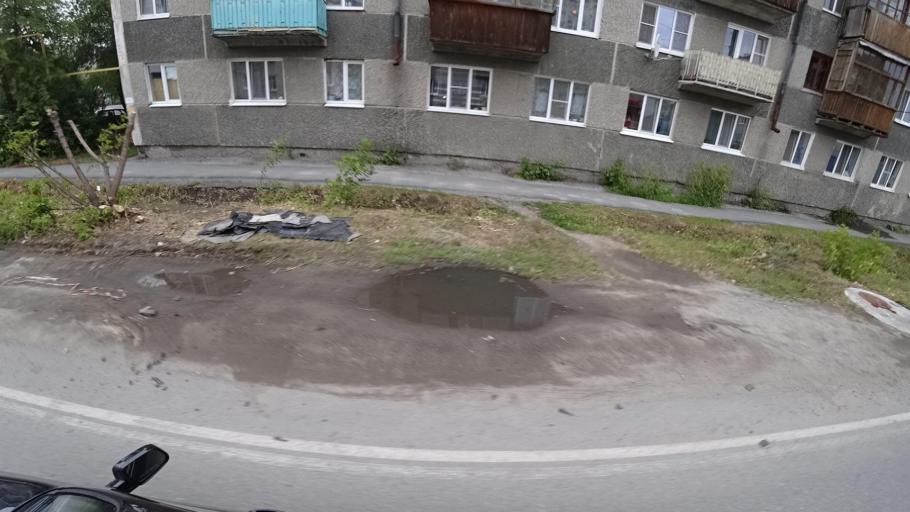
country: RU
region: Sverdlovsk
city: Kamyshlov
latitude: 56.8391
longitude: 62.7147
